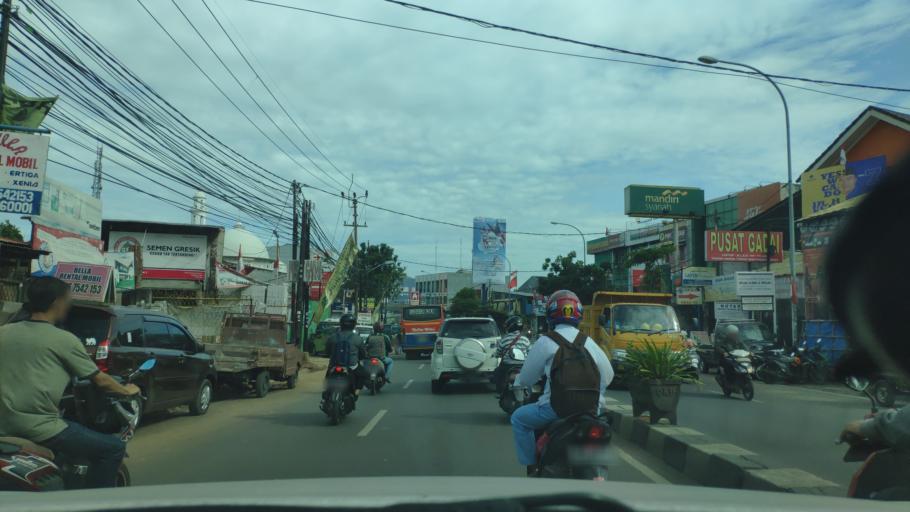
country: ID
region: West Java
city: Ciputat
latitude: -6.2255
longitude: 106.7117
